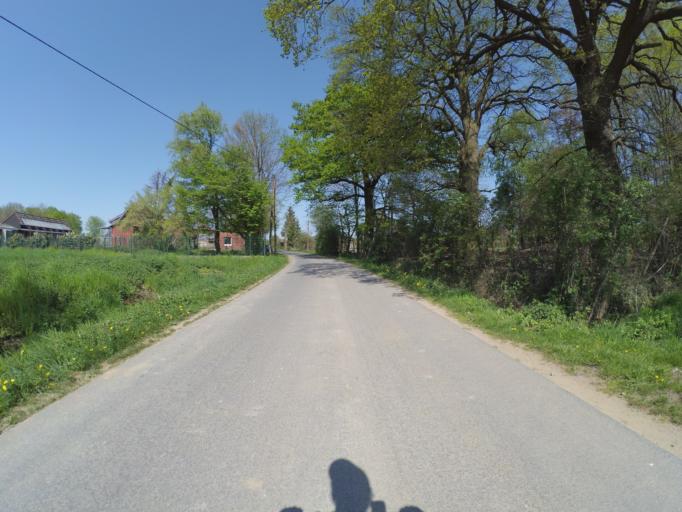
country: DE
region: North Rhine-Westphalia
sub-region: Regierungsbezirk Munster
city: Ascheberg
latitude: 51.8107
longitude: 7.5959
